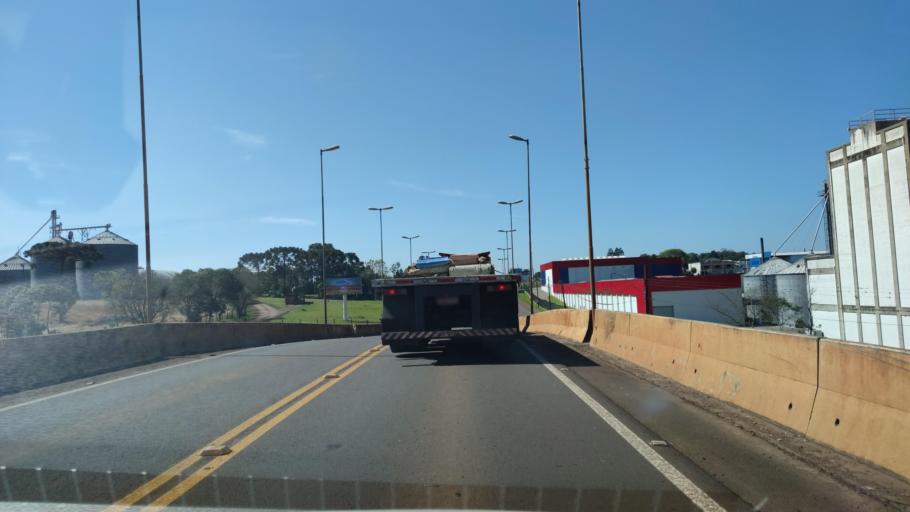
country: BR
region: Santa Catarina
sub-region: Sao Lourenco Do Oeste
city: Sao Lourenco dOeste
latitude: -26.3472
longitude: -52.8528
